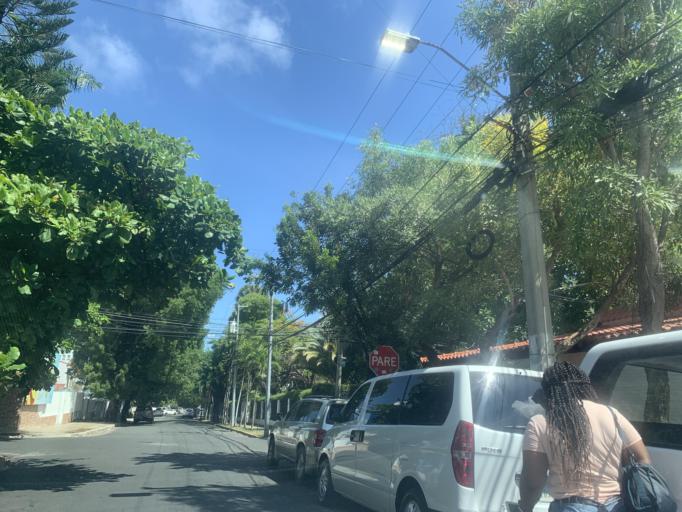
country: DO
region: Nacional
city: Ciudad Nueva
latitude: 18.4670
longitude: -69.9001
